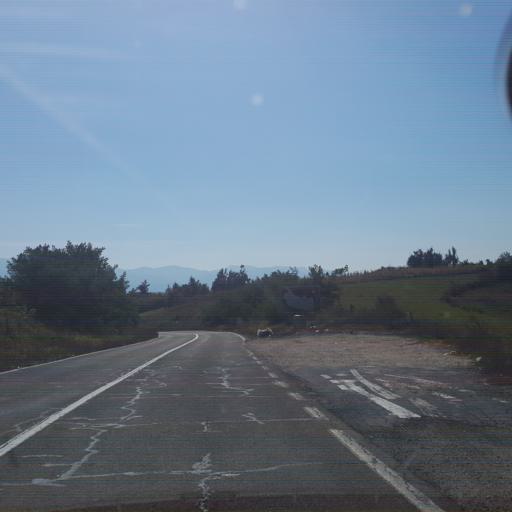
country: RS
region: Central Serbia
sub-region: Zajecarski Okrug
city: Knjazevac
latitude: 43.4752
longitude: 22.2283
